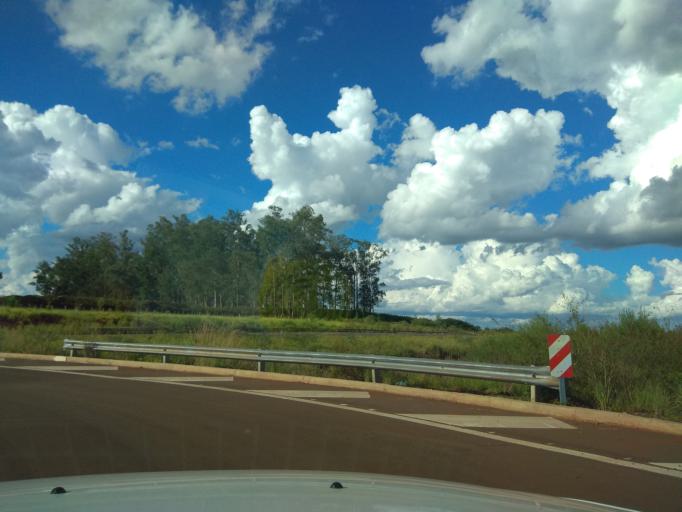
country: AR
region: Misiones
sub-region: Departamento de Candelaria
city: Candelaria
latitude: -27.4653
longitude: -55.7095
